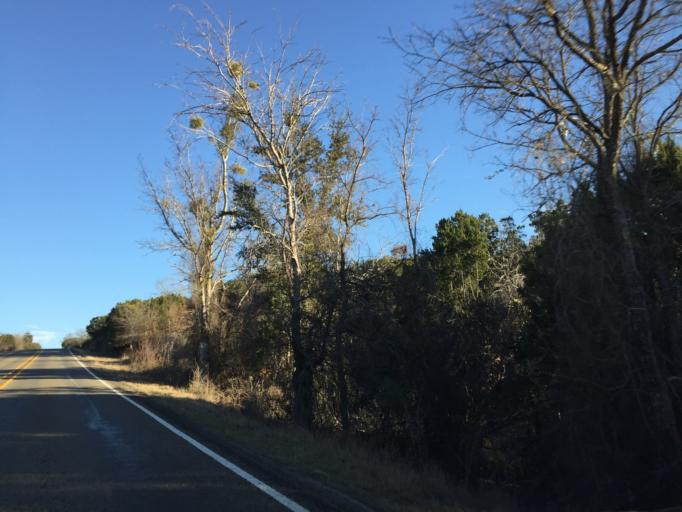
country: US
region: Texas
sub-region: Travis County
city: Lago Vista
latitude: 30.5234
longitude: -98.0833
